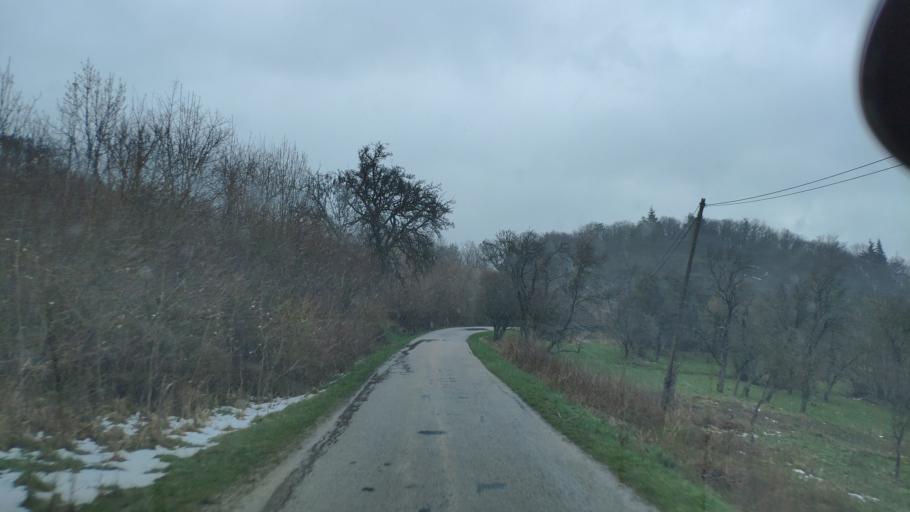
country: SK
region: Nitriansky
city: Stara Tura
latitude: 48.8246
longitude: 17.7022
